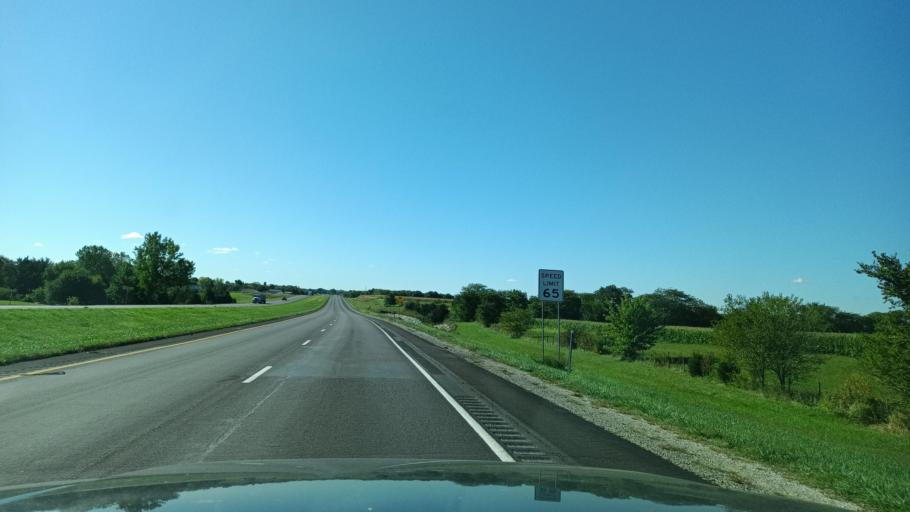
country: US
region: Iowa
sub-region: Lee County
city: Keokuk
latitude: 40.4647
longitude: -91.4448
